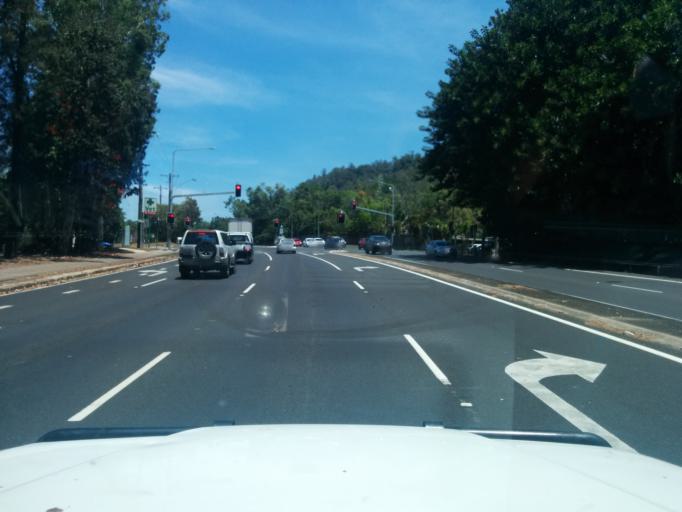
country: AU
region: Queensland
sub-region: Cairns
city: Redlynch
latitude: -16.9042
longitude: 145.7092
